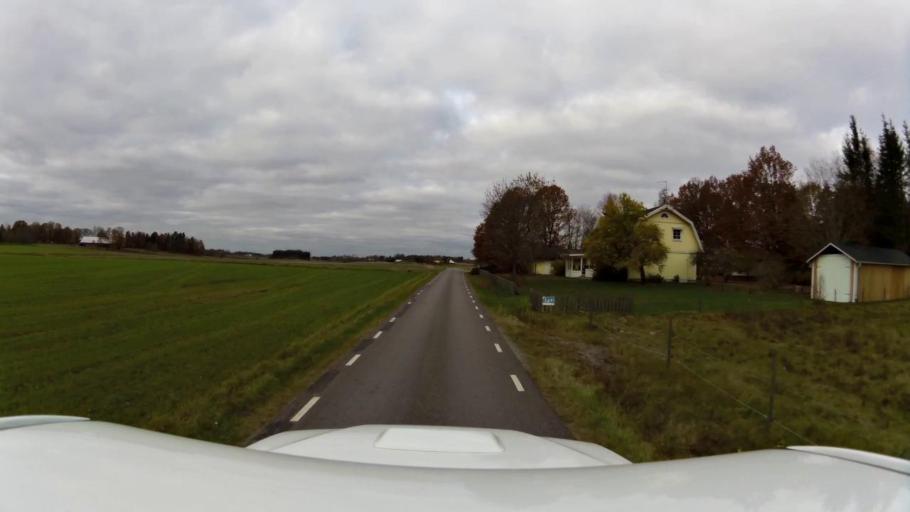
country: SE
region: OEstergoetland
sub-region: Linkopings Kommun
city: Linghem
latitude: 58.3936
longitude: 15.7996
